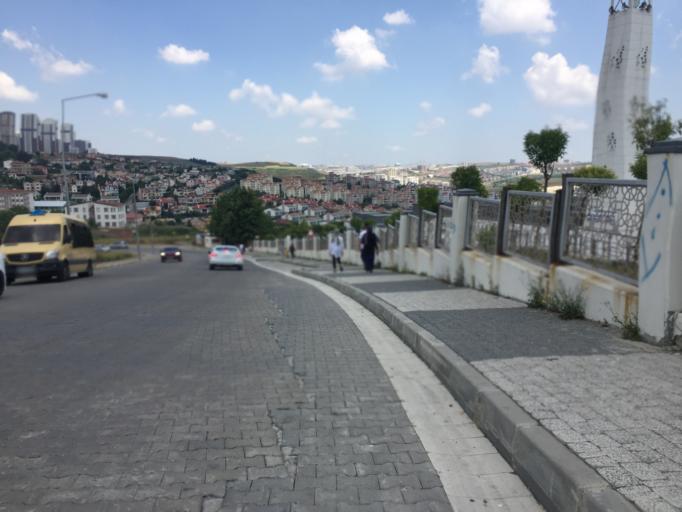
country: TR
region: Istanbul
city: Esenyurt
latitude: 41.0778
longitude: 28.6658
